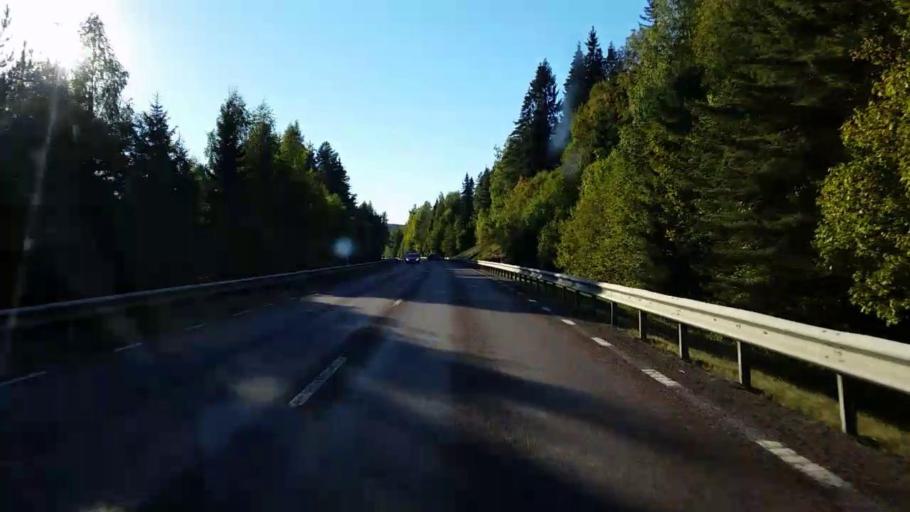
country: SE
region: Gaevleborg
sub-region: Hudiksvalls Kommun
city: Delsbo
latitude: 61.8072
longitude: 16.4273
